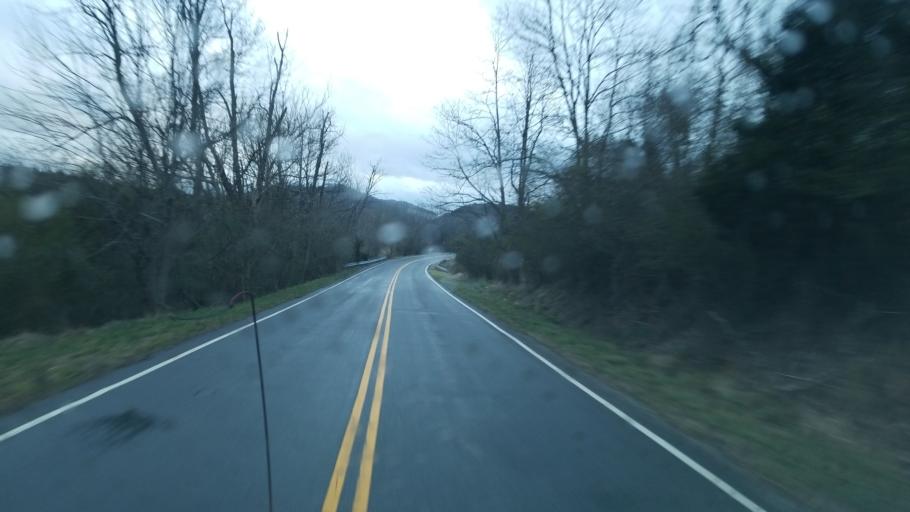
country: US
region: Virginia
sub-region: Giles County
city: Narrows
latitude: 37.1988
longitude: -80.8265
